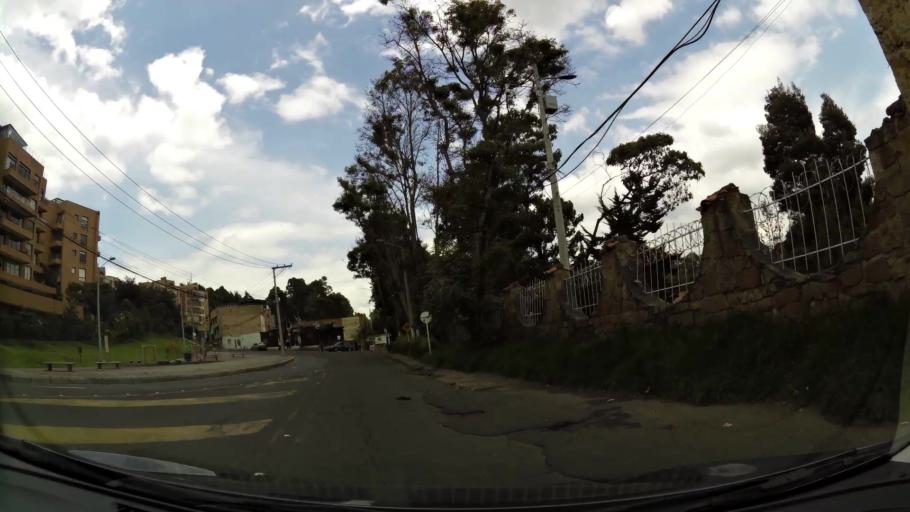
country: CO
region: Cundinamarca
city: Cota
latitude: 4.7333
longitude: -74.0741
